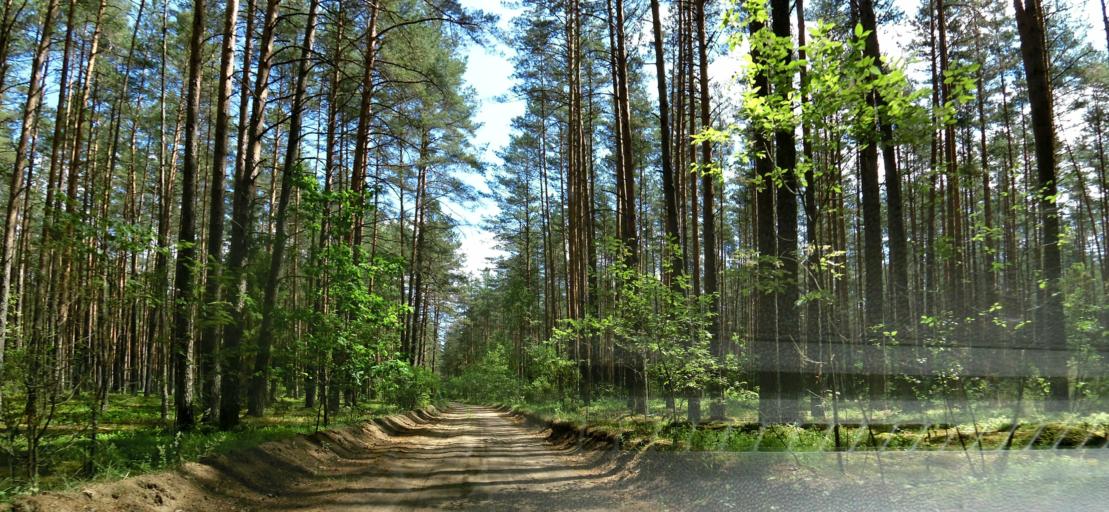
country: LT
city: Nemencine
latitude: 54.8283
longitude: 25.4207
